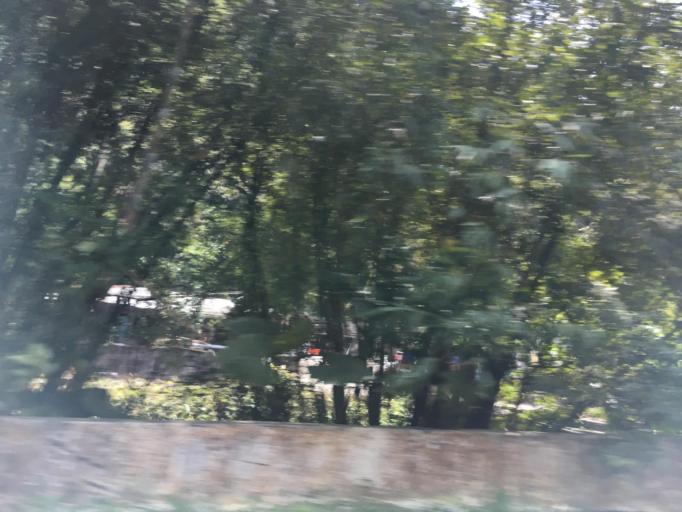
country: TW
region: Taiwan
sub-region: Yilan
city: Yilan
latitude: 24.8153
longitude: 121.7391
